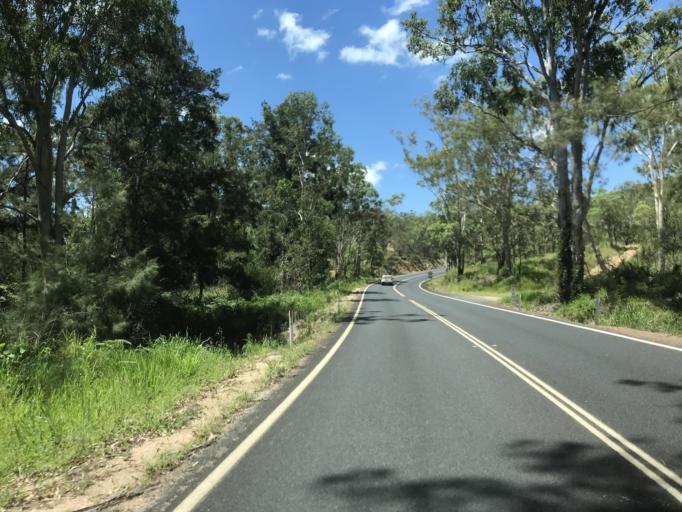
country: AU
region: Queensland
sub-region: Tablelands
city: Atherton
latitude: -17.4026
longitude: 145.3901
